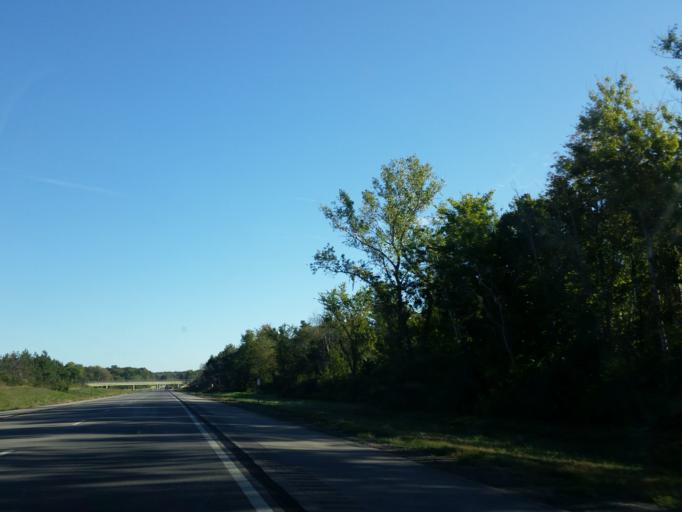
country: US
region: New York
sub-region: Erie County
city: Angola
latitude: 42.6234
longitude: -79.0030
